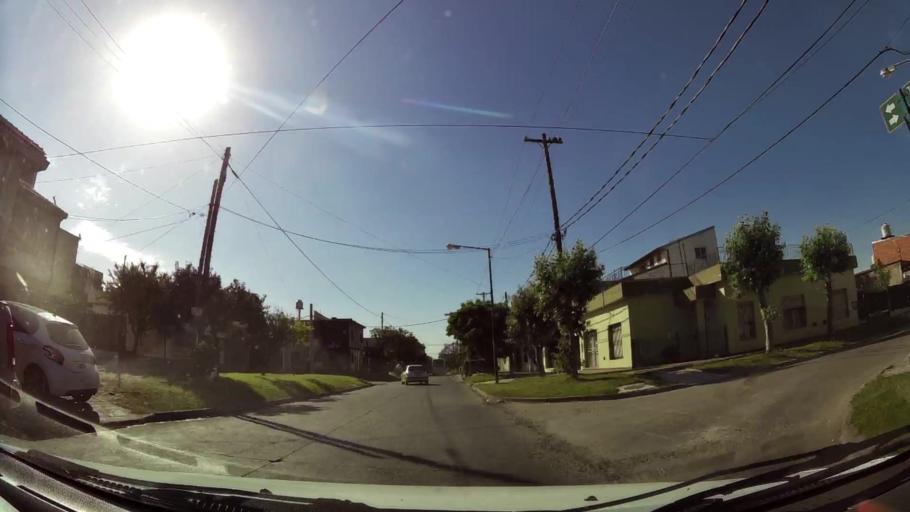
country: AR
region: Buenos Aires
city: Hurlingham
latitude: -34.5590
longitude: -58.6029
